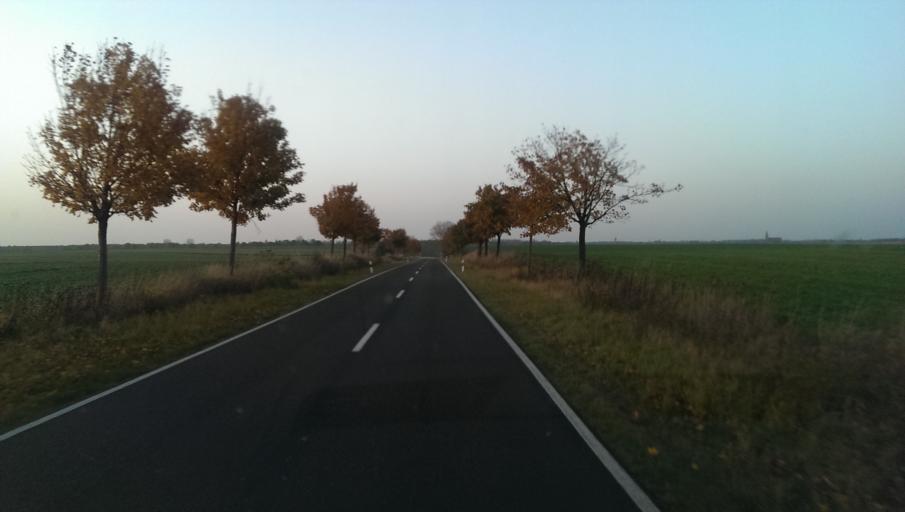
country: DE
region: Brandenburg
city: Juterbog
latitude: 51.9618
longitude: 13.0818
